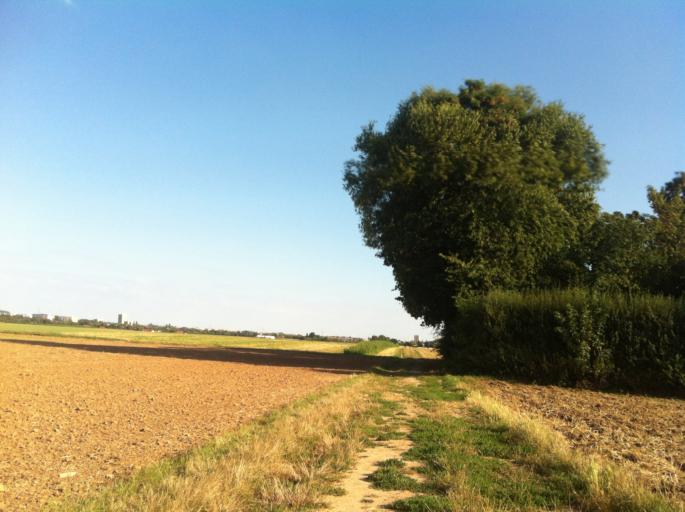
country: DE
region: Rheinland-Pfalz
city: Klein-Winternheim
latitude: 49.9830
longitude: 8.2143
